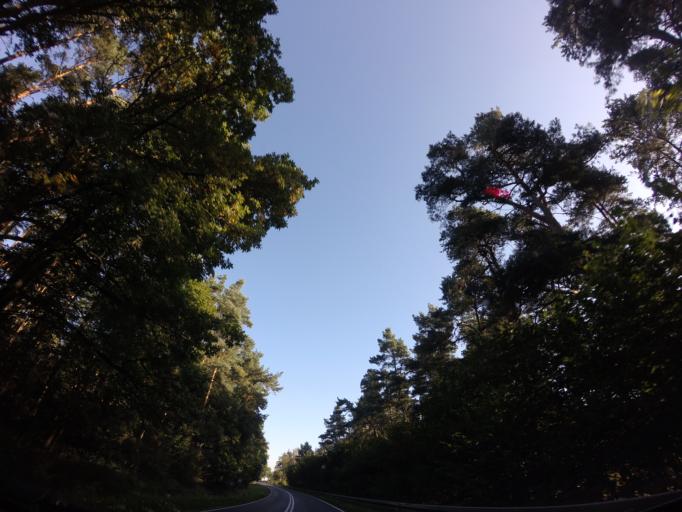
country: PL
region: West Pomeranian Voivodeship
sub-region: Powiat stargardzki
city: Stara Dabrowa
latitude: 53.4000
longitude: 15.1004
